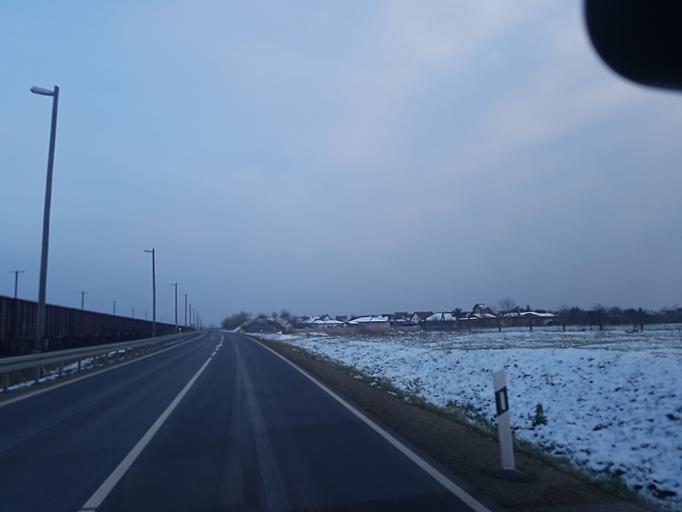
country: DE
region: Brandenburg
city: Muhlberg
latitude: 51.4398
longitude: 13.2274
